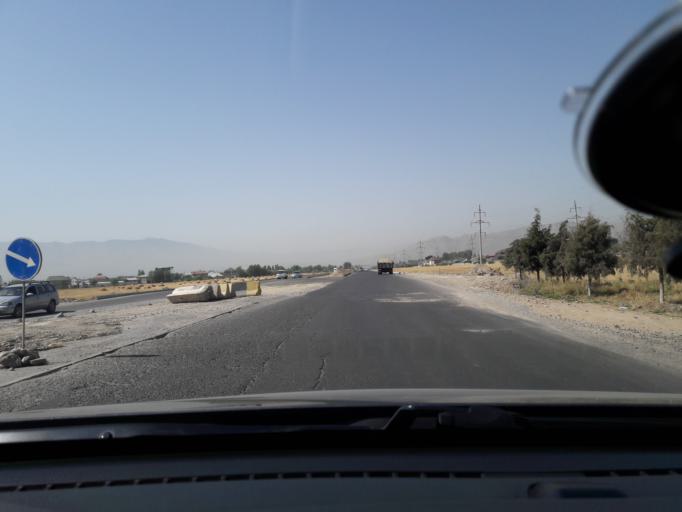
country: TJ
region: Dushanbe
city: Dushanbe
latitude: 38.4974
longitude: 68.7547
